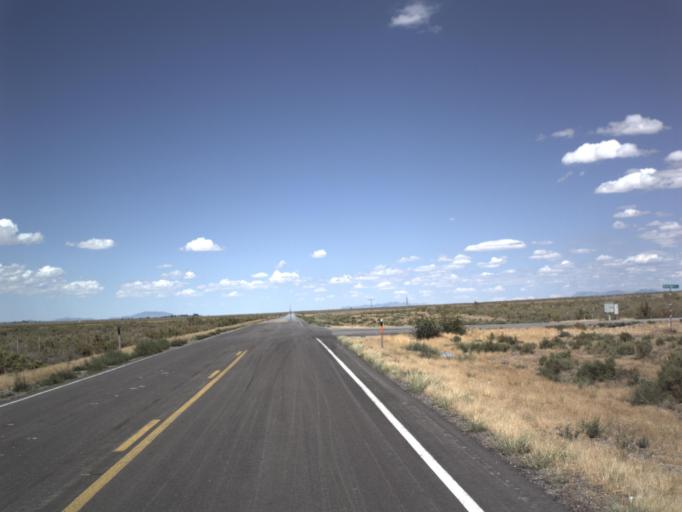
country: US
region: Utah
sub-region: Millard County
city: Delta
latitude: 39.3256
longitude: -112.4845
